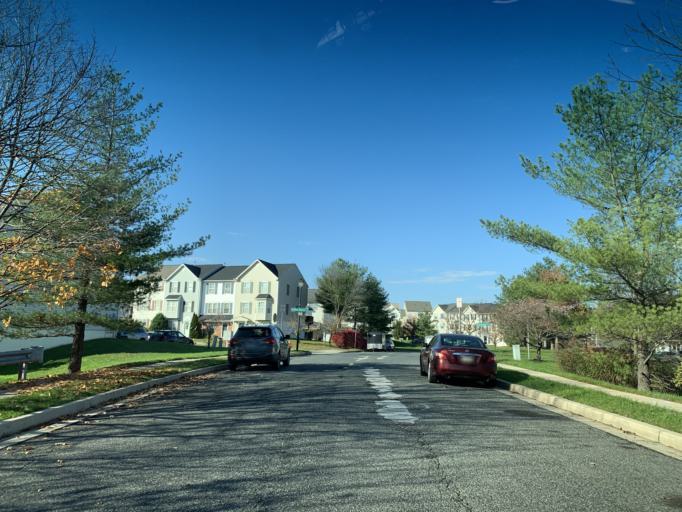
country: US
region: Maryland
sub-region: Baltimore County
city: Middle River
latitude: 39.3526
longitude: -76.4424
